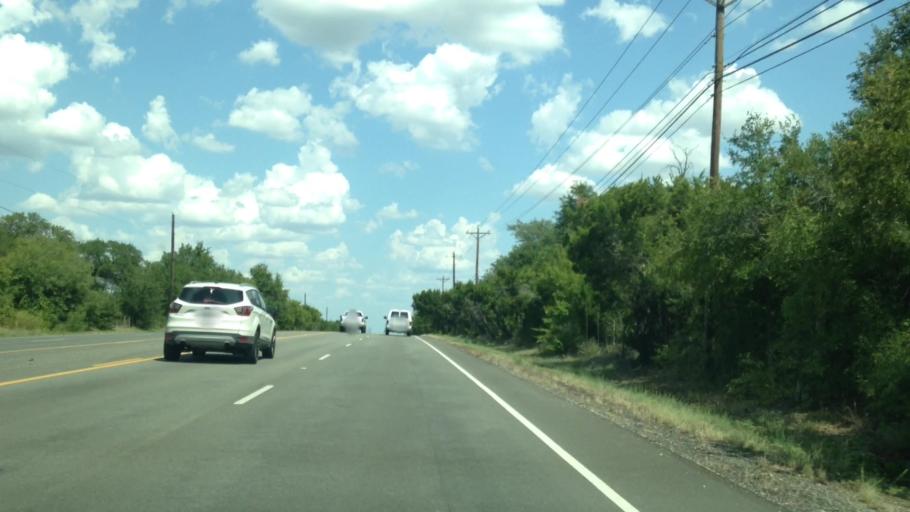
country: US
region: Texas
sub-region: Williamson County
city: Georgetown
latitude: 30.6340
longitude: -97.7227
